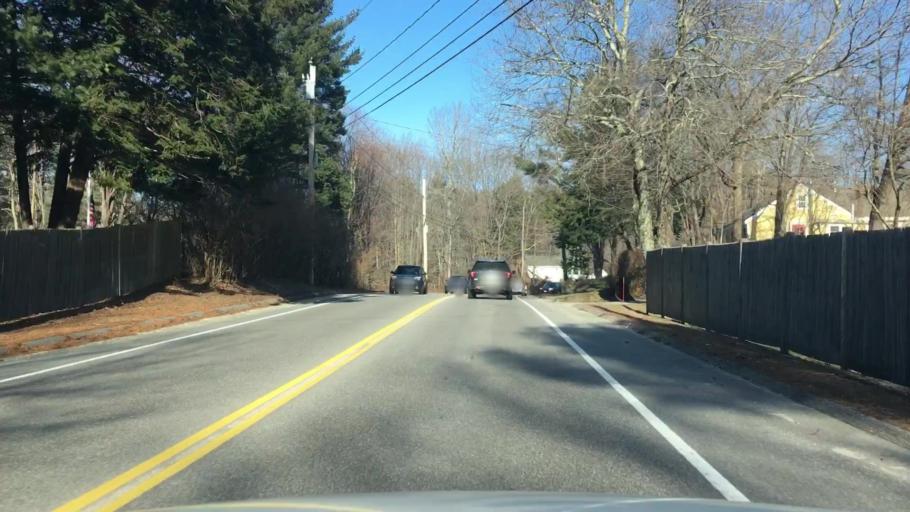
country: US
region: Maine
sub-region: Cumberland County
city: Falmouth
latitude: 43.7200
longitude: -70.2640
